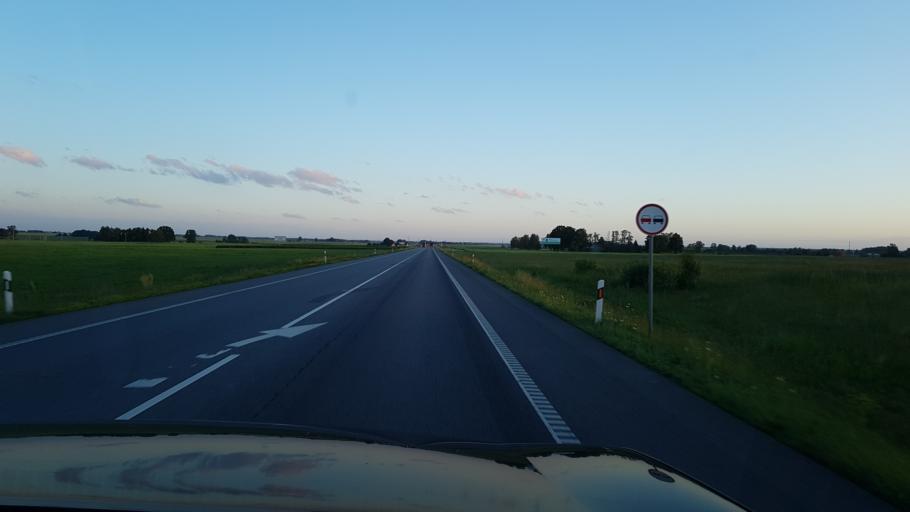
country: LT
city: Kazlu Ruda
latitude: 54.6534
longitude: 23.4969
